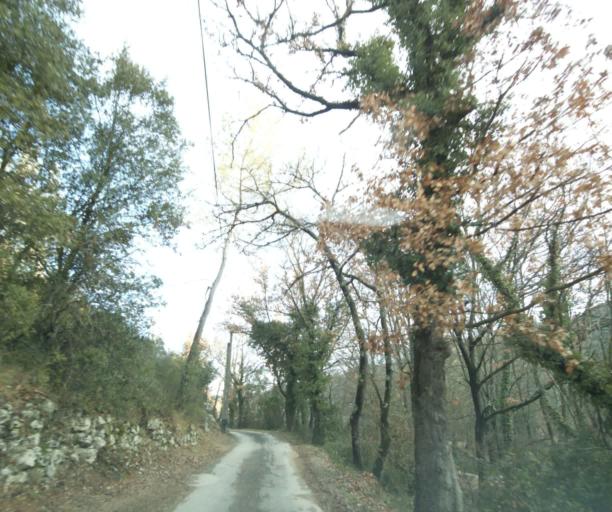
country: FR
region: Provence-Alpes-Cote d'Azur
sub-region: Departement du Var
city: Tourves
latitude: 43.3925
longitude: 5.9344
